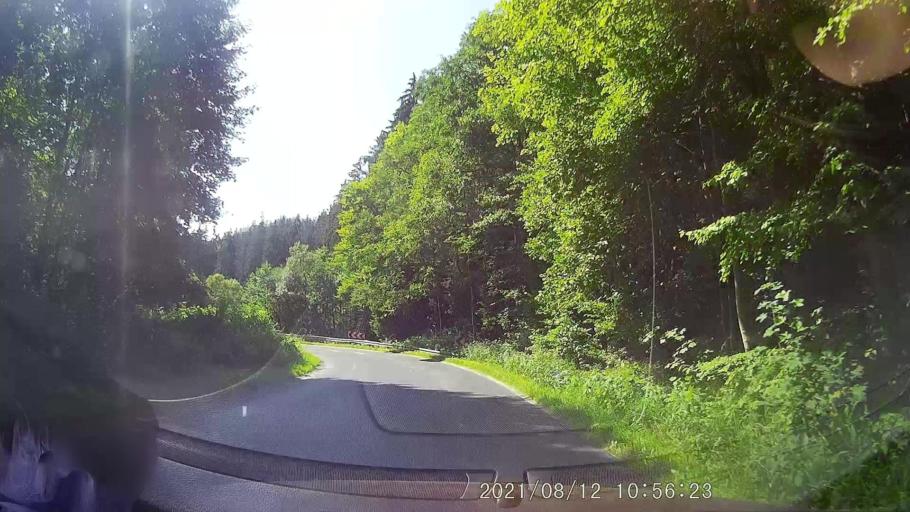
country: PL
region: Lower Silesian Voivodeship
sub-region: Powiat klodzki
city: Polanica-Zdroj
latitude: 50.4009
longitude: 16.4853
